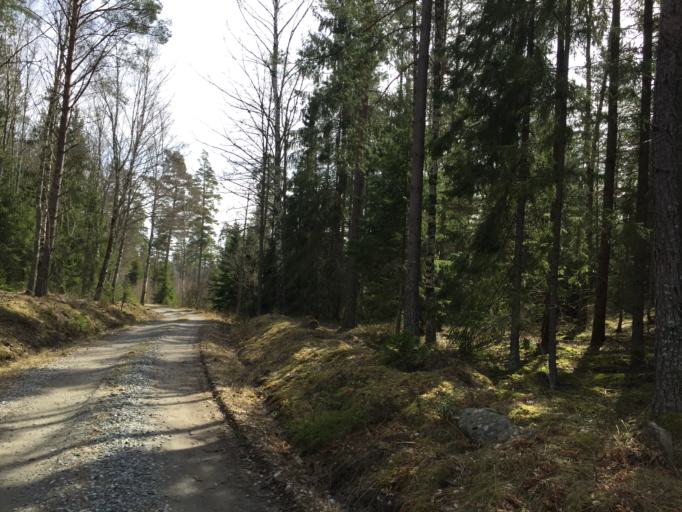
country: SE
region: Stockholm
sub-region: Salems Kommun
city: Ronninge
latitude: 59.2527
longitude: 17.6789
